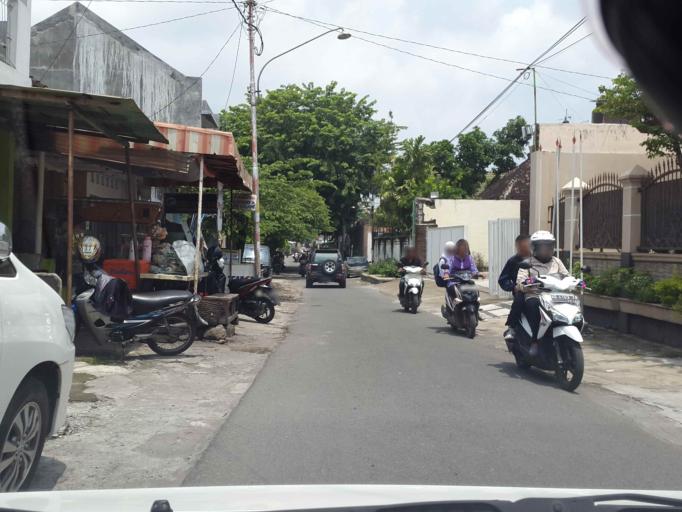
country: ID
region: Central Java
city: Grogol
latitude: -7.5835
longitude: 110.8319
